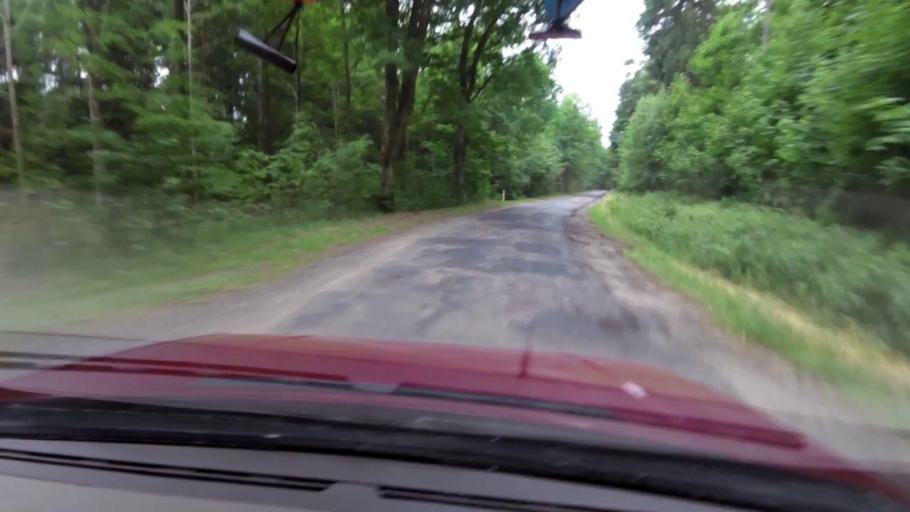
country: PL
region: Pomeranian Voivodeship
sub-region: Powiat slupski
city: Kepice
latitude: 54.1934
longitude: 16.8063
